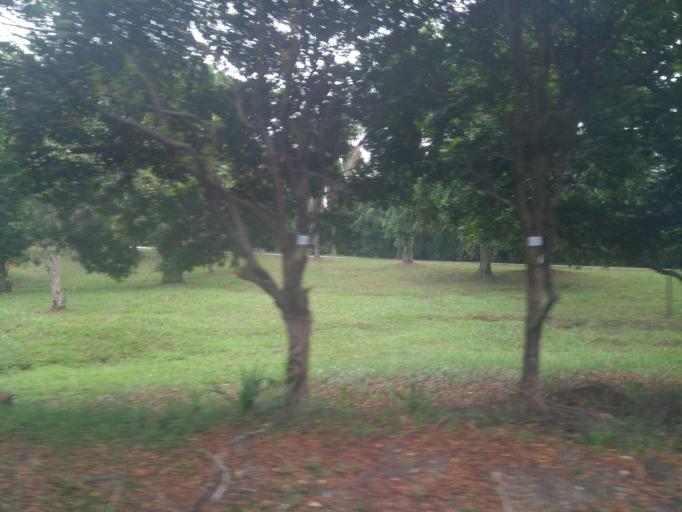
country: MY
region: Johor
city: Johor Bahru
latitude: 1.4895
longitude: 103.7384
